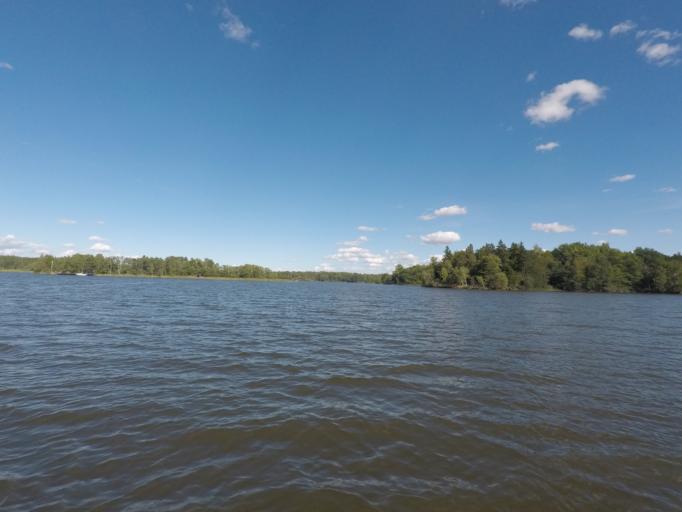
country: SE
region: Soedermanland
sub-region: Eskilstuna Kommun
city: Torshalla
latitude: 59.4790
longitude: 16.4124
